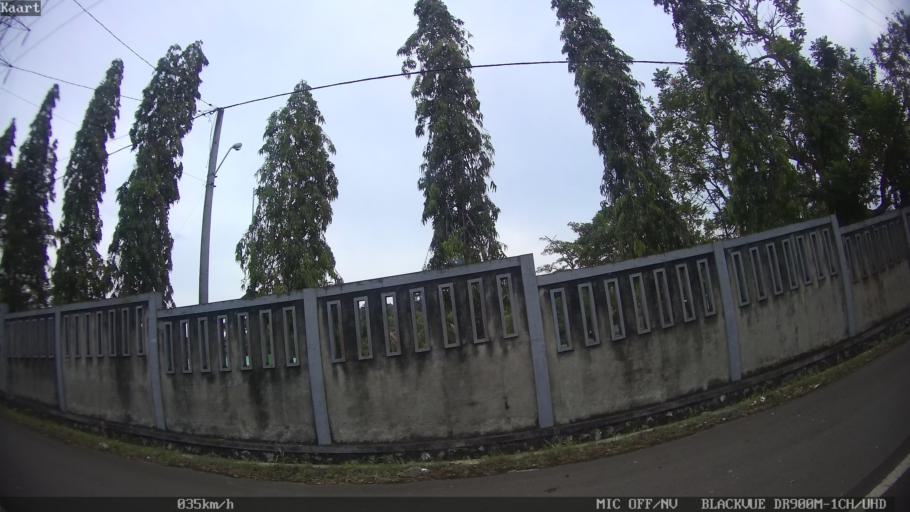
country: ID
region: Lampung
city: Bandarlampung
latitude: -5.4351
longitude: 105.2266
